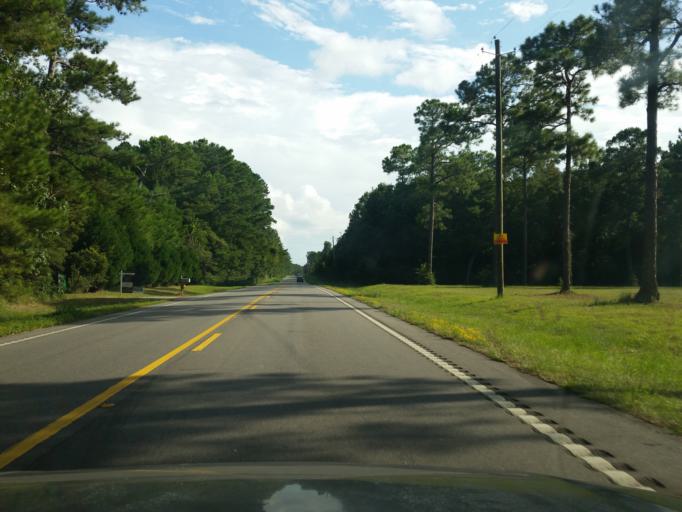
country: US
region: Alabama
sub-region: Mobile County
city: Bayou La Batre
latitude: 30.4144
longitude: -88.1070
